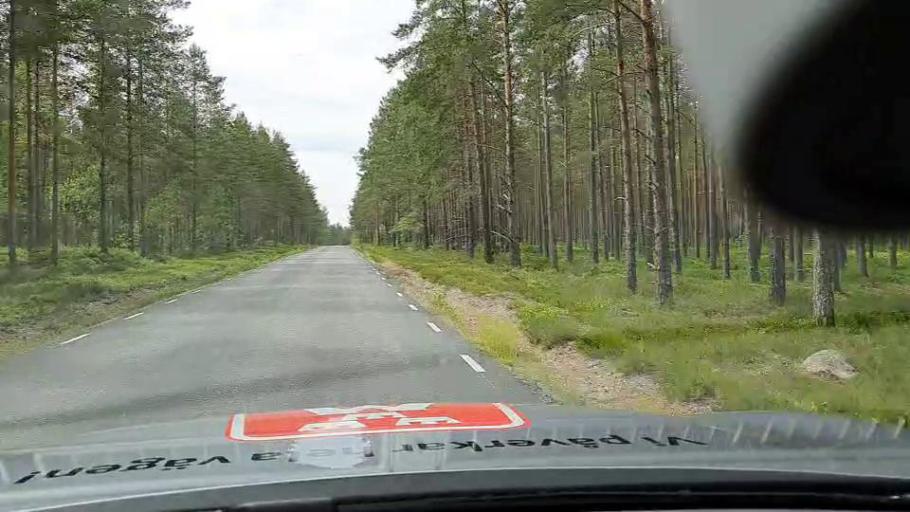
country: SE
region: Soedermanland
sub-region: Eskilstuna Kommun
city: Arla
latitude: 59.2318
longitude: 16.7355
